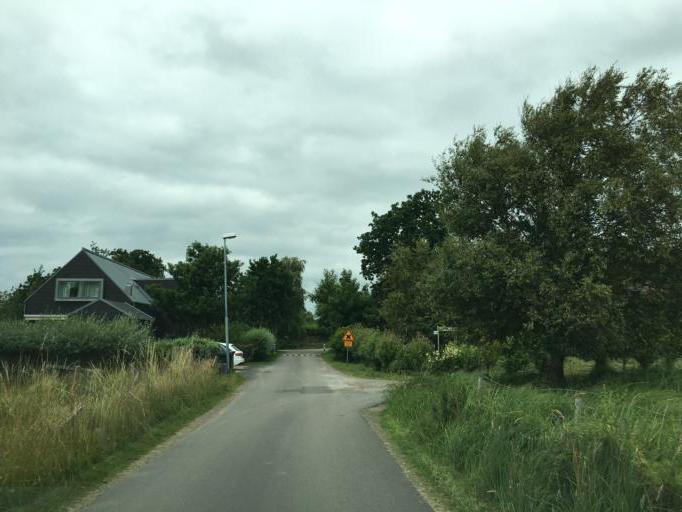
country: SE
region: Skane
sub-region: Angelholms Kommun
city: Vejbystrand
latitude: 56.3267
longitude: 12.7610
